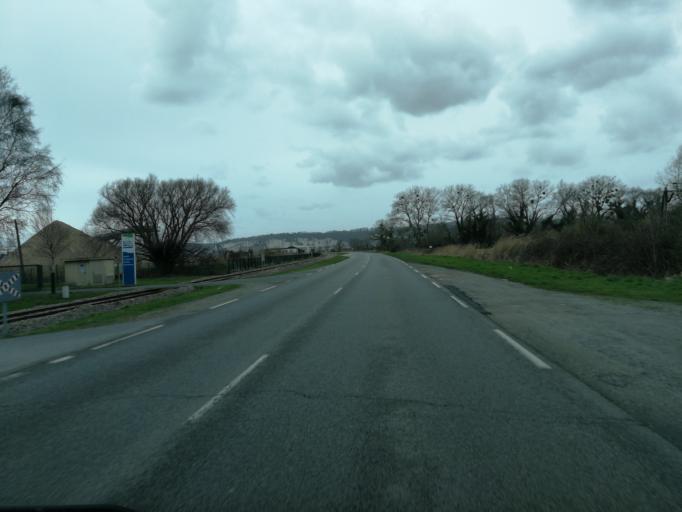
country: FR
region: Haute-Normandie
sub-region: Departement de l'Eure
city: Quillebeuf-sur-Seine
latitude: 49.4887
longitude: 0.5099
